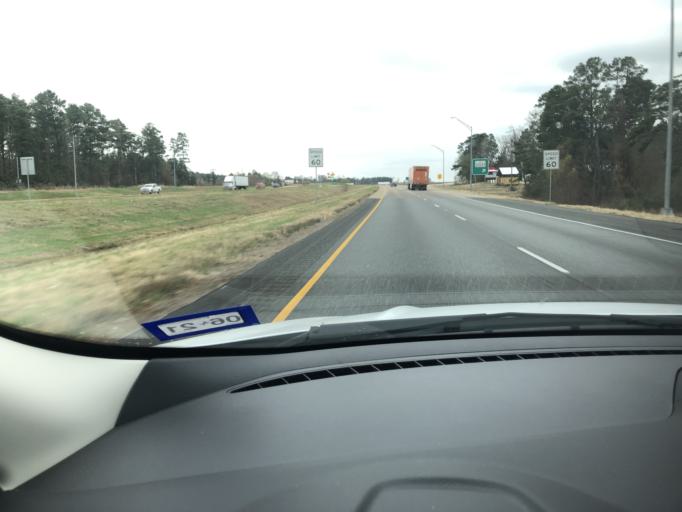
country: US
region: Texas
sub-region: Angelina County
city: Redland
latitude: 31.4172
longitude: -94.7225
